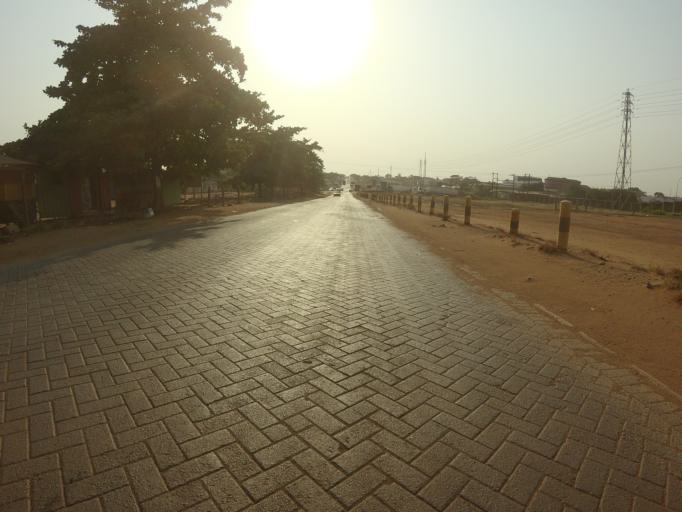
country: GH
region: Greater Accra
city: Tema
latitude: 5.6648
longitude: 0.0050
